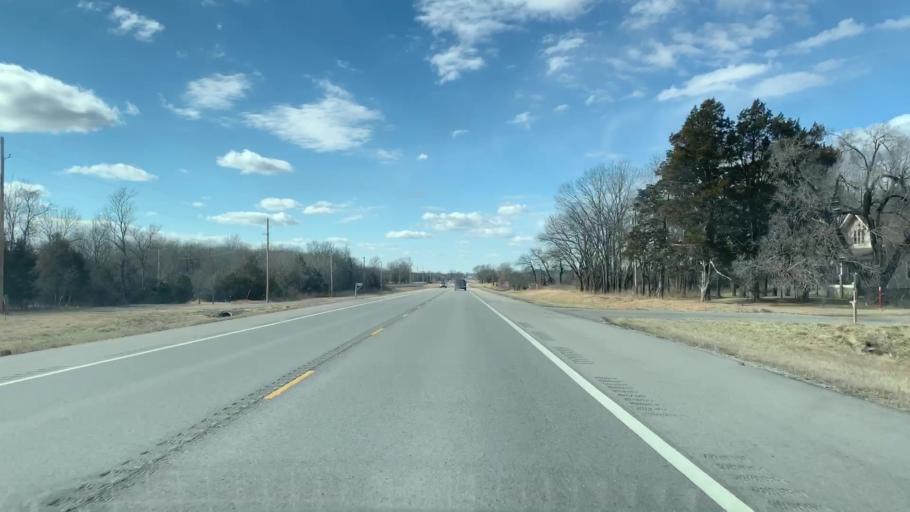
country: US
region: Kansas
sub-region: Labette County
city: Oswego
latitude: 37.3401
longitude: -95.0604
